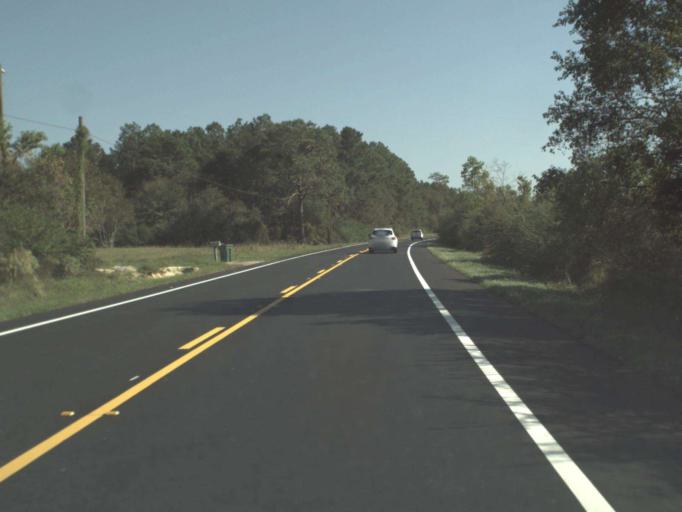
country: US
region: Alabama
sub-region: Covington County
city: Florala
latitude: 30.8723
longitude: -86.2587
